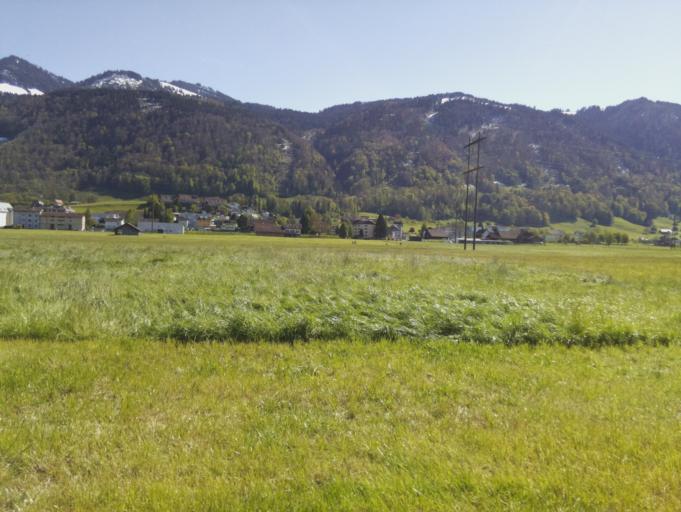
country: CH
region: Schwyz
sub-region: Bezirk March
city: Schubelbach
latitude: 47.1800
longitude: 8.9389
